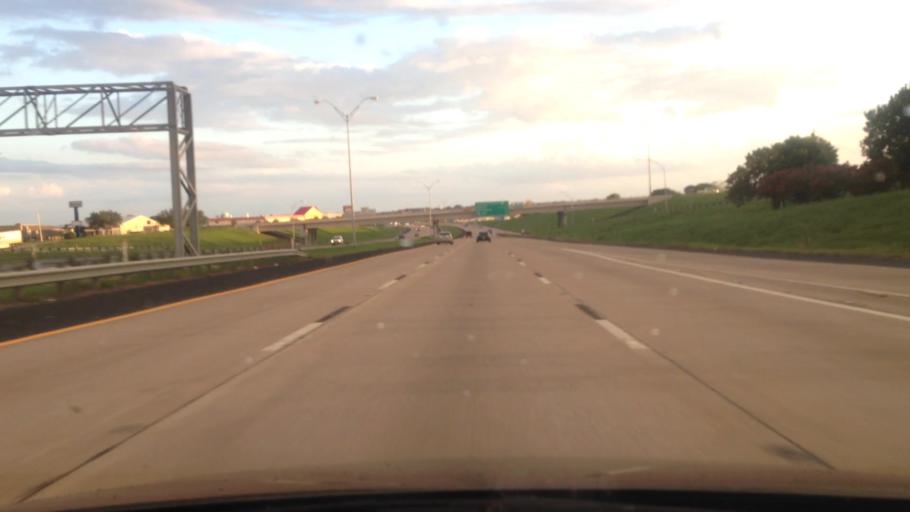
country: US
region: Texas
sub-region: Tarrant County
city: White Settlement
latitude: 32.7358
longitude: -97.4815
